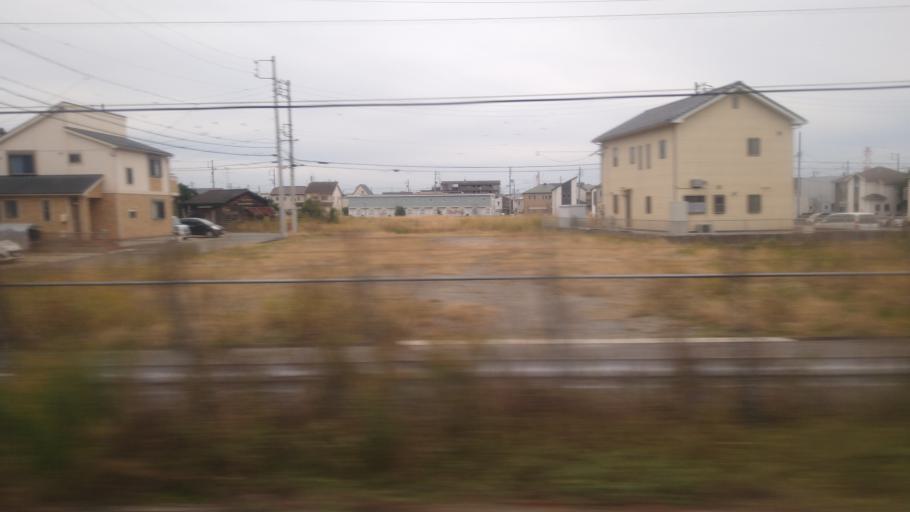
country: JP
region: Aichi
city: Kasugai
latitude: 35.2623
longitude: 137.0210
